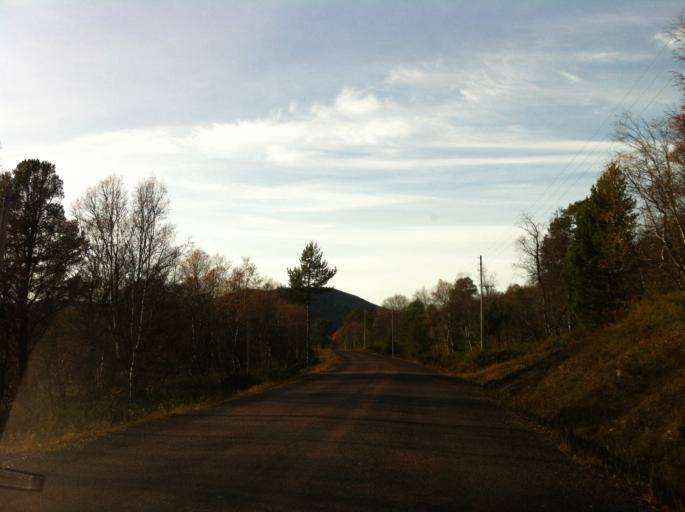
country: NO
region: Hedmark
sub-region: Engerdal
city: Engerdal
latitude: 62.0835
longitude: 12.1001
